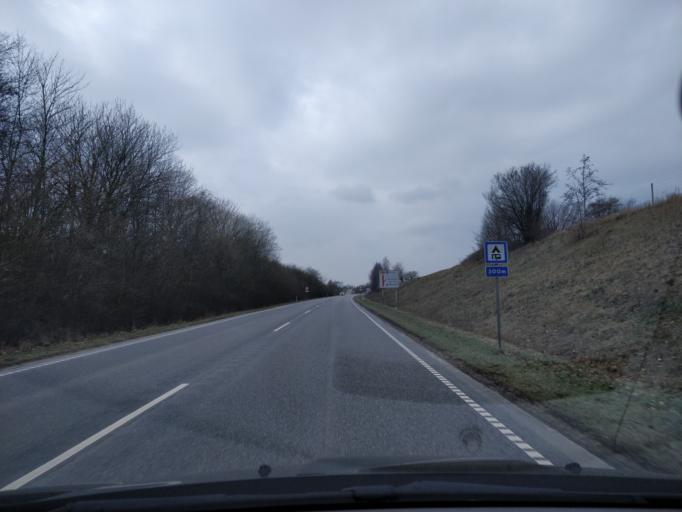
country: DK
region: South Denmark
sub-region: Vejle Kommune
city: Brejning
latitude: 55.6306
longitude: 9.6957
